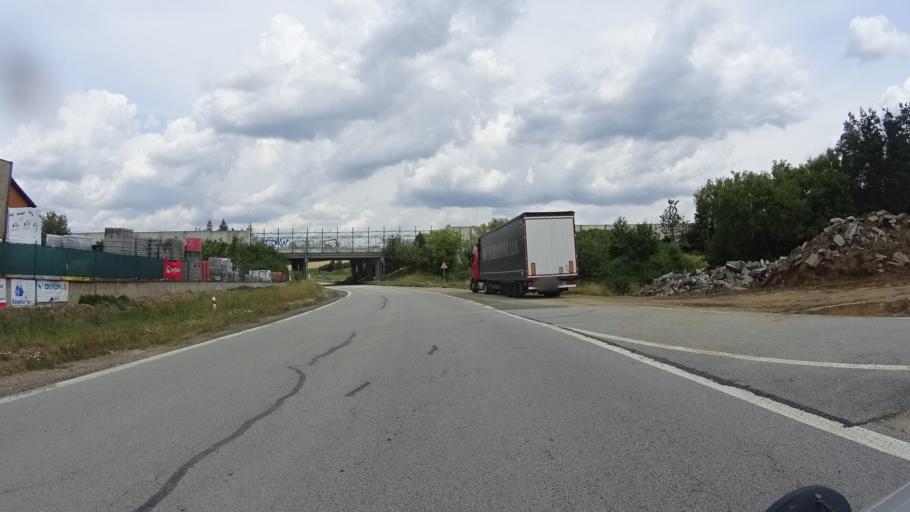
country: CZ
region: Vysocina
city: Merin
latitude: 49.3961
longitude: 15.8832
